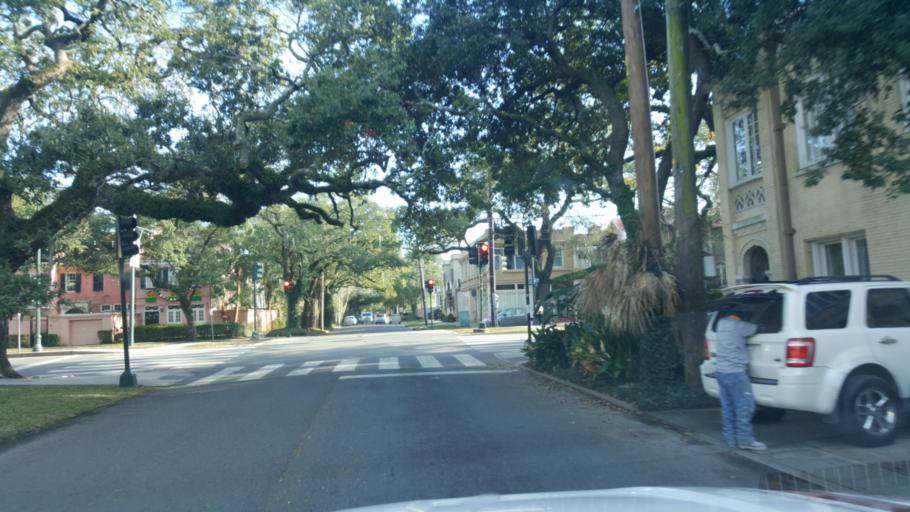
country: US
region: Louisiana
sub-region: Orleans Parish
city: New Orleans
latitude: 29.9313
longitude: -90.0862
